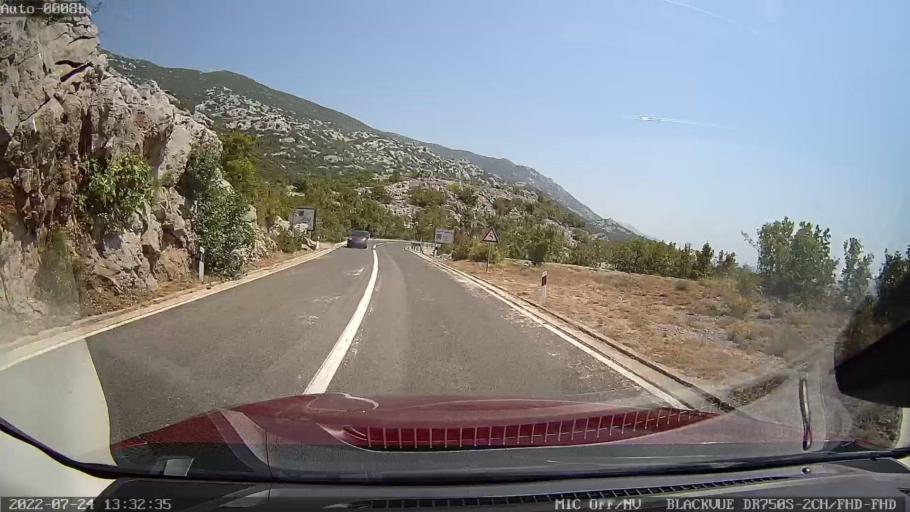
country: HR
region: Licko-Senjska
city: Karlobag
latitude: 44.5902
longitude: 14.9959
